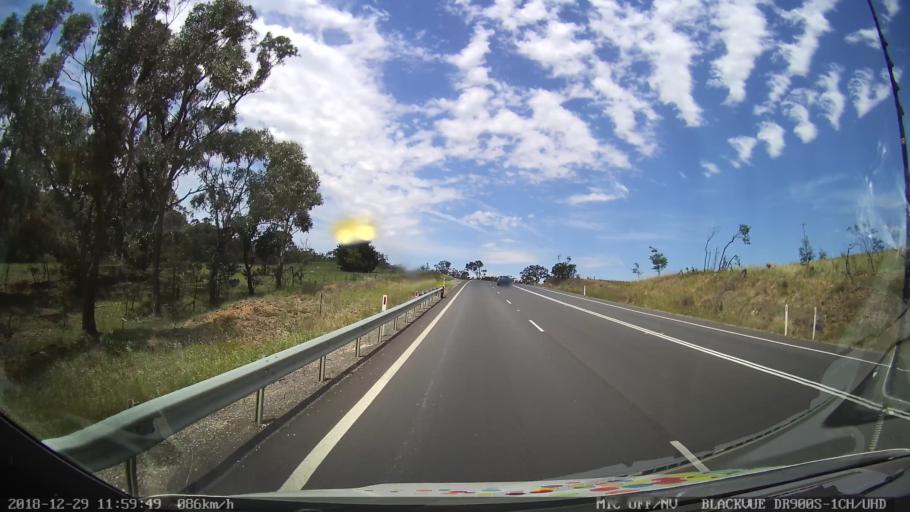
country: AU
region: New South Wales
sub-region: Palerang
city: Bungendore
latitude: -35.3154
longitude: 149.3984
